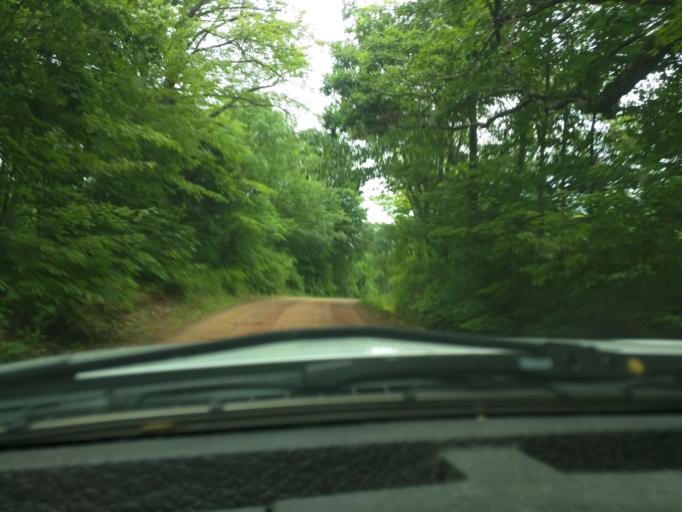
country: US
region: Arkansas
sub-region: Madison County
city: Huntsville
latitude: 35.8828
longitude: -93.5439
